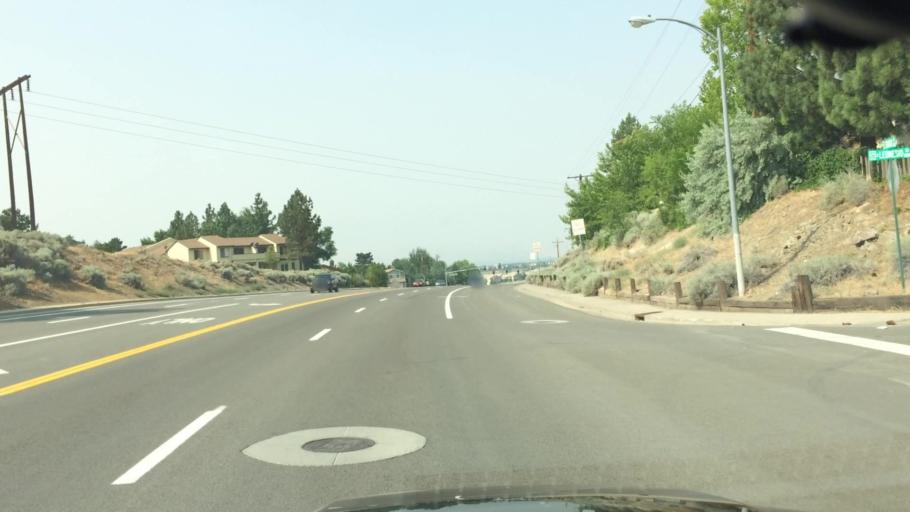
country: US
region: Nevada
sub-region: Washoe County
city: Sun Valley
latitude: 39.5653
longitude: -119.7841
